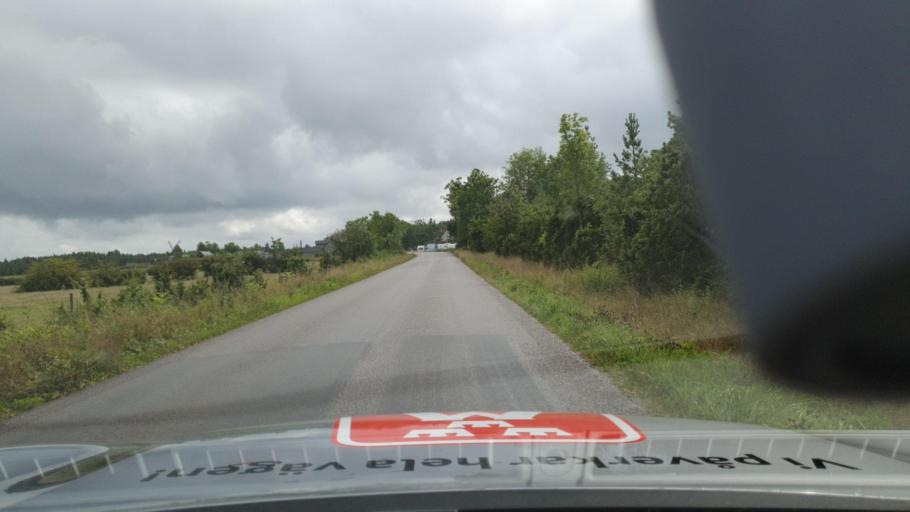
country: SE
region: Gotland
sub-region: Gotland
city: Slite
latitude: 57.6864
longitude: 18.7643
